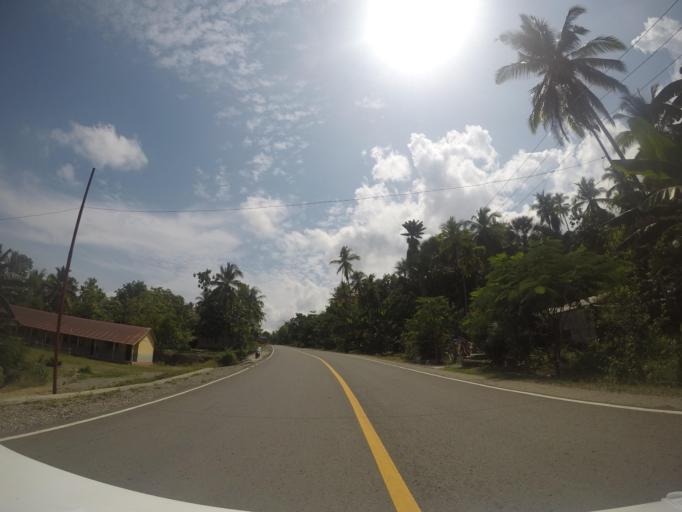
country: TL
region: Baucau
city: Baucau
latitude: -8.4876
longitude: 126.3382
